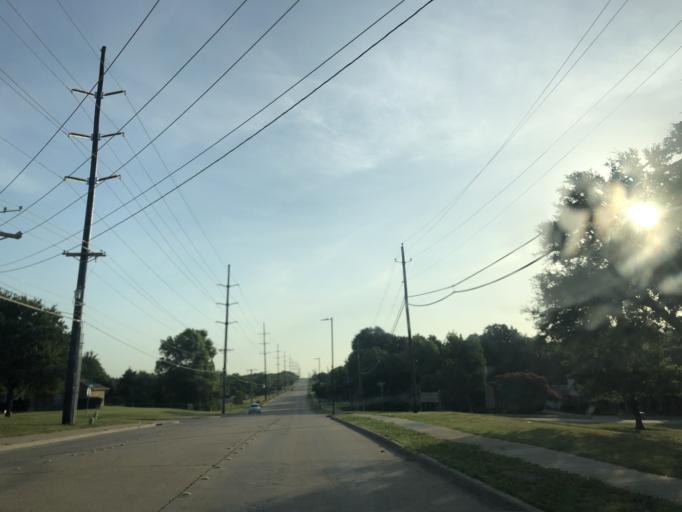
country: US
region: Texas
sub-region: Dallas County
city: Rowlett
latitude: 32.8669
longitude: -96.6030
